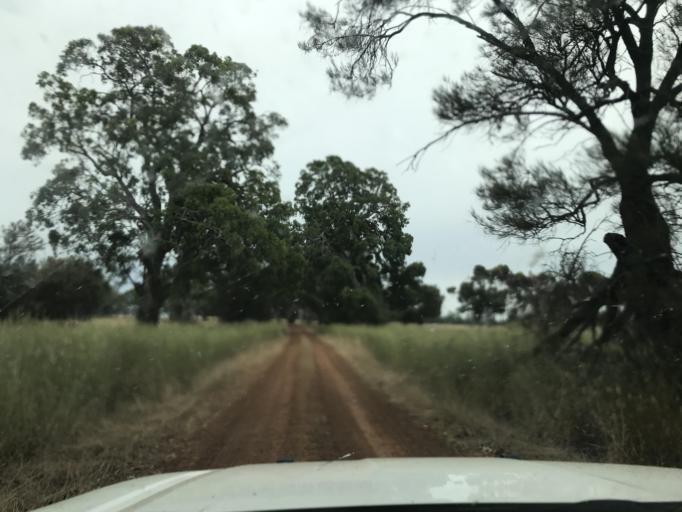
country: AU
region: Victoria
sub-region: Horsham
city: Horsham
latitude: -37.0653
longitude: 141.6785
